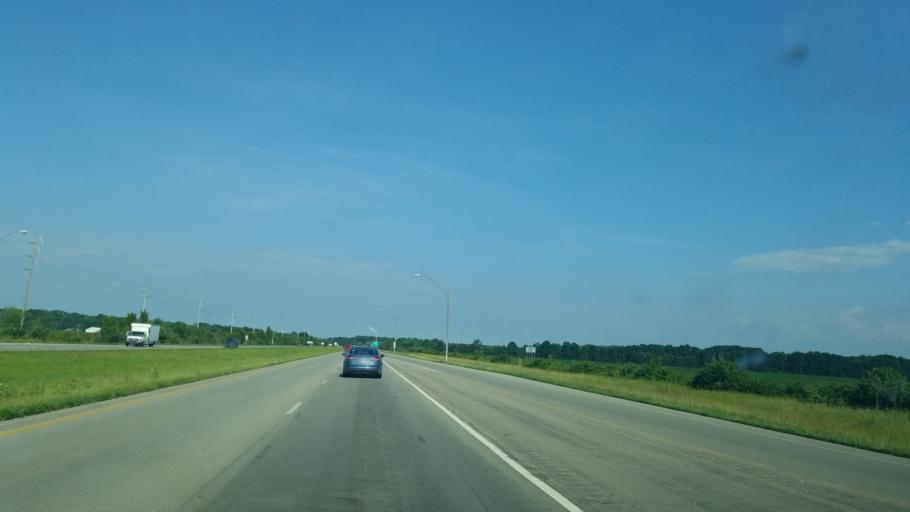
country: US
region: Ohio
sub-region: Clermont County
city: Williamsburg
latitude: 39.0695
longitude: -84.0910
